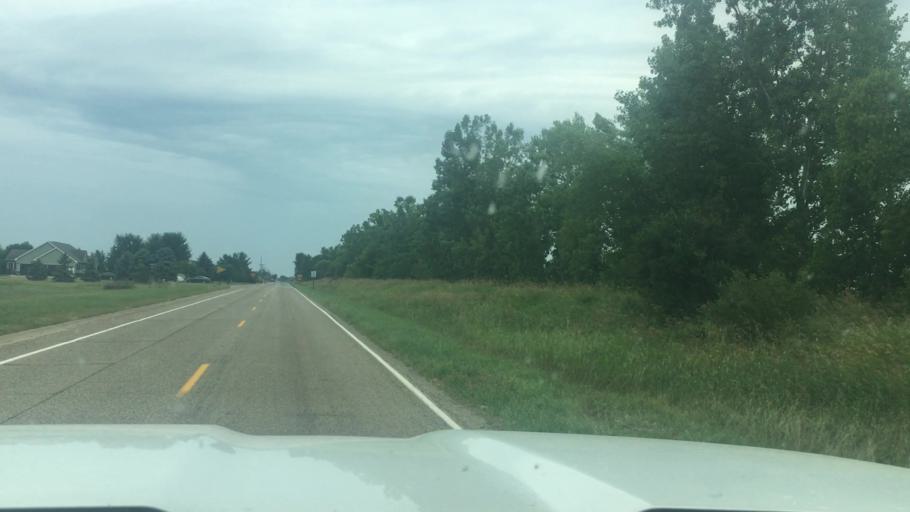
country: US
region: Michigan
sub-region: Clinton County
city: Saint Johns
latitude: 43.0495
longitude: -84.4842
